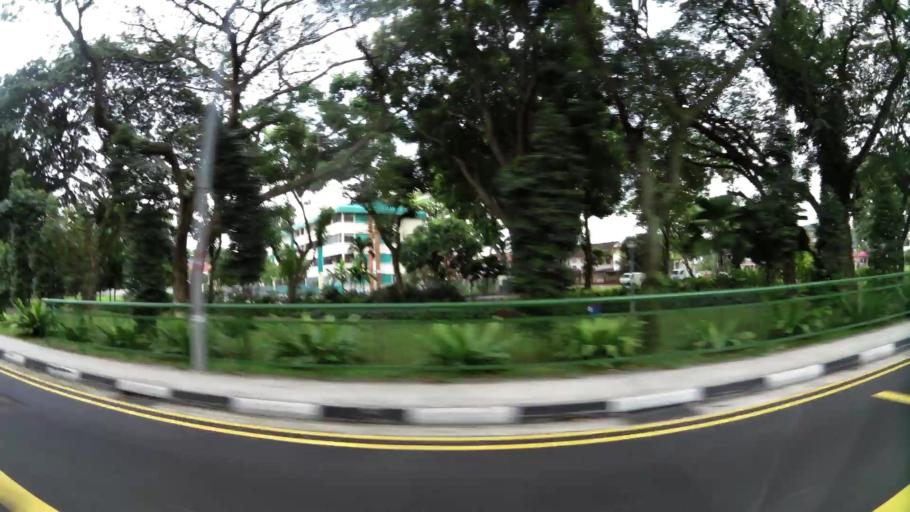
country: SG
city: Singapore
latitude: 1.3299
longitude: 103.8795
